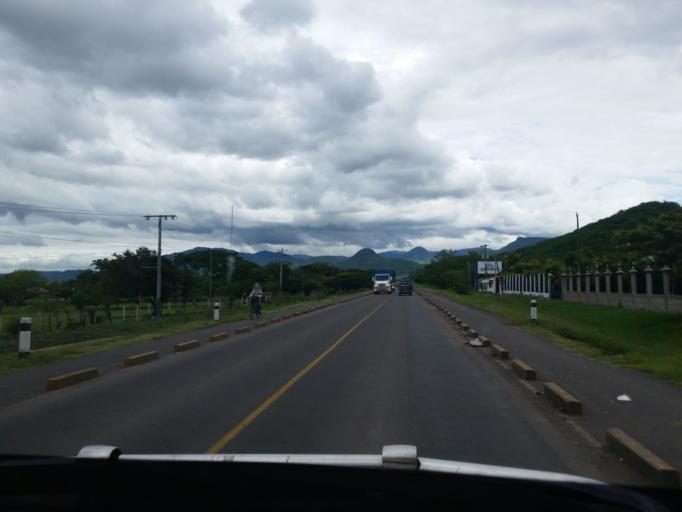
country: NI
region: Matagalpa
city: Ciudad Dario
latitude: 12.8653
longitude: -86.0922
